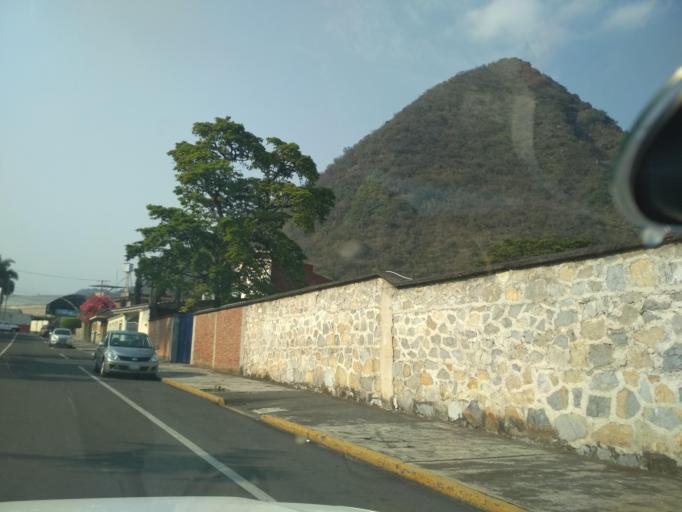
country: MX
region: Veracruz
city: Orizaba
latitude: 18.8561
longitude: -97.0890
